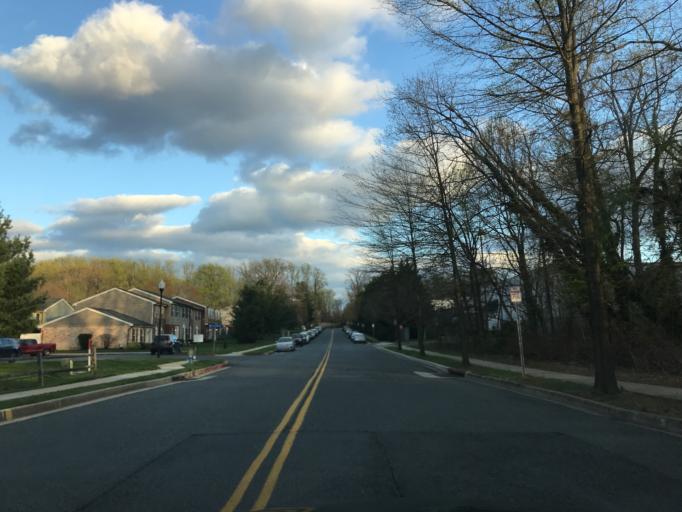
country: US
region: Maryland
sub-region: Harford County
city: Bel Air
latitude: 39.5251
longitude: -76.3466
